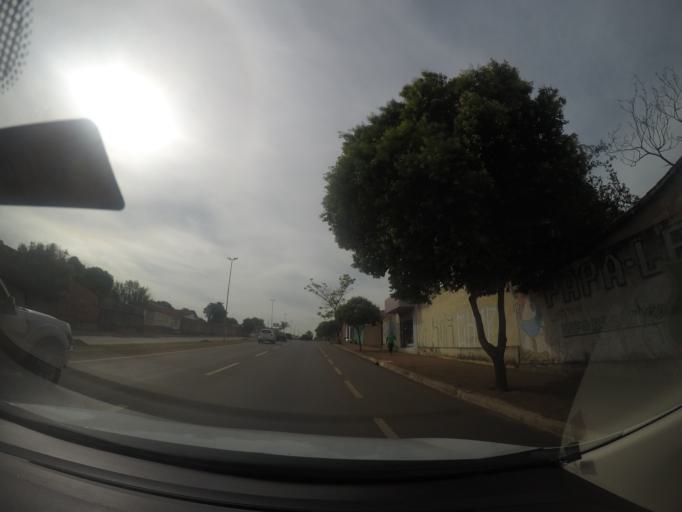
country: BR
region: Goias
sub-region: Goiania
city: Goiania
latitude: -16.6587
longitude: -49.2942
